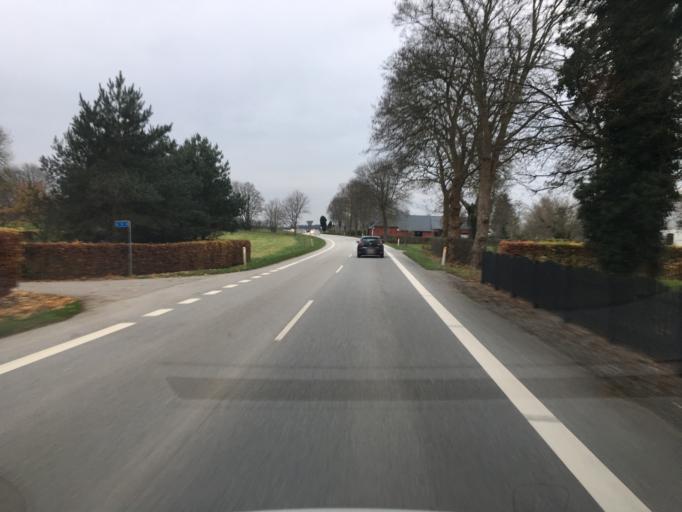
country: DK
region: South Denmark
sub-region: Aabenraa Kommune
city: Tinglev
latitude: 55.0073
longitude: 9.2526
